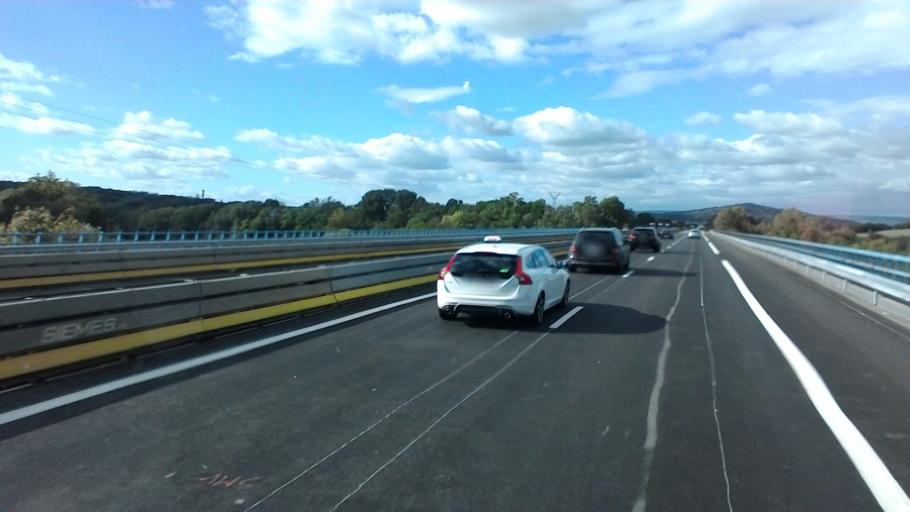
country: FR
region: Lorraine
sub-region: Departement de Meurthe-et-Moselle
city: Belleville
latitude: 48.8235
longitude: 6.1026
